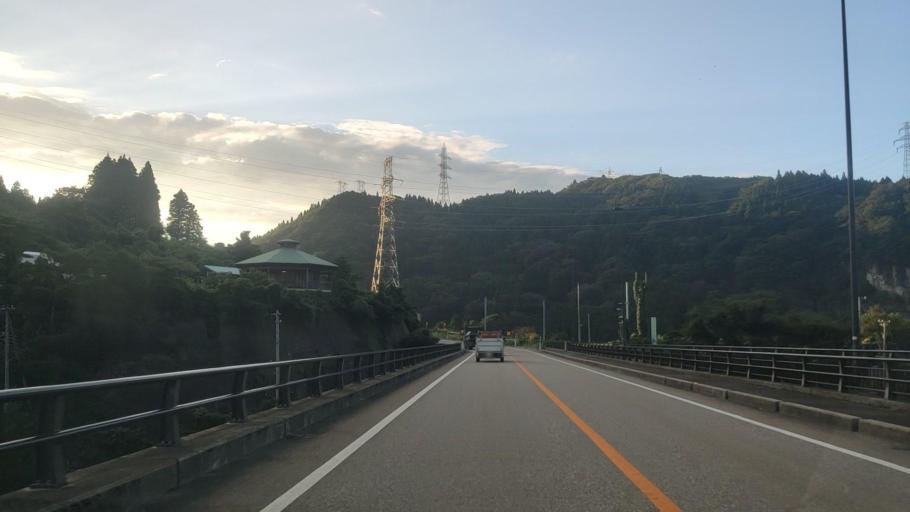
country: JP
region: Toyama
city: Nanto-shi
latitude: 36.5631
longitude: 137.0058
